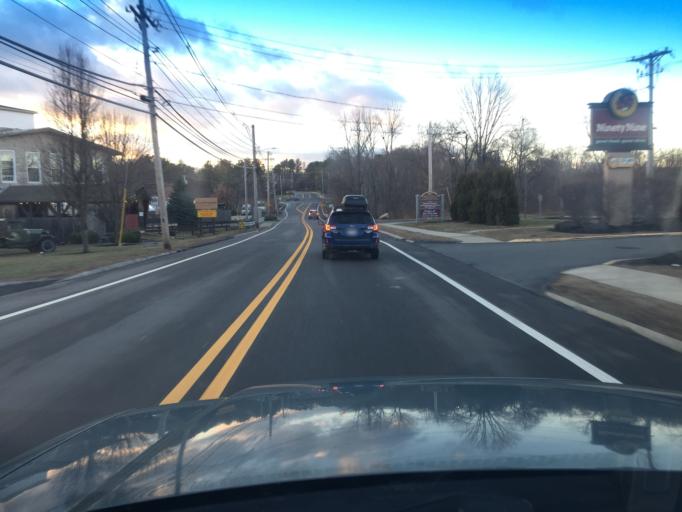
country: US
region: Massachusetts
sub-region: Norfolk County
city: Franklin
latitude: 42.0903
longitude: -71.4320
